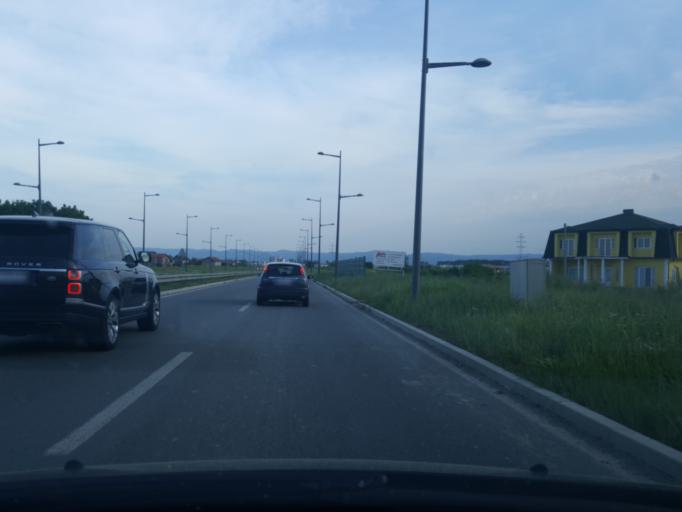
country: RS
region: Autonomna Pokrajina Vojvodina
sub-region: Juznobacki Okrug
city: Novi Sad
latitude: 45.2999
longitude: 19.8077
